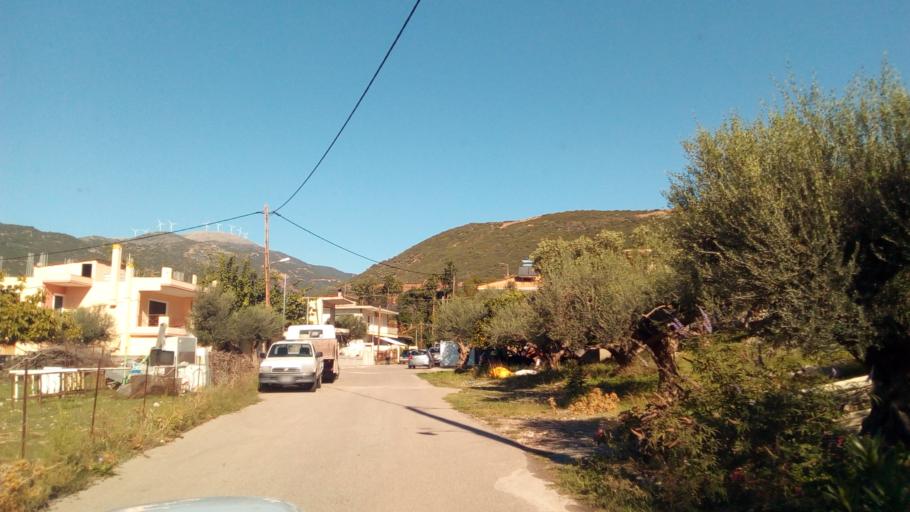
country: GR
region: West Greece
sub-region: Nomos Aitolias kai Akarnanias
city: Nafpaktos
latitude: 38.4063
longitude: 21.8554
